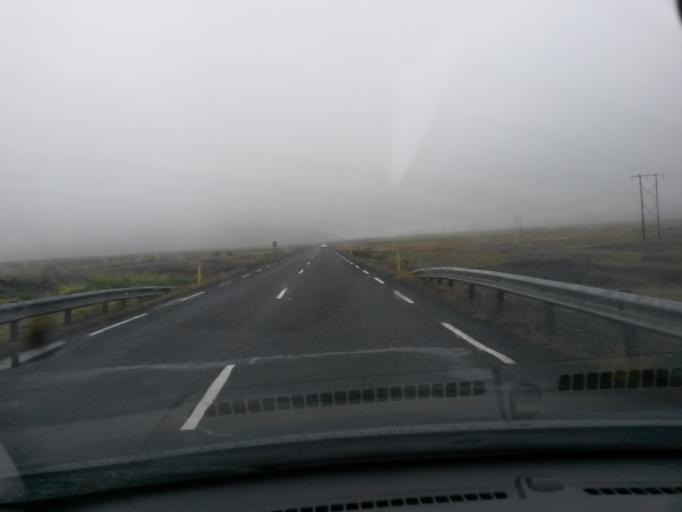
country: IS
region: South
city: Vestmannaeyjar
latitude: 63.4615
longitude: -19.2281
